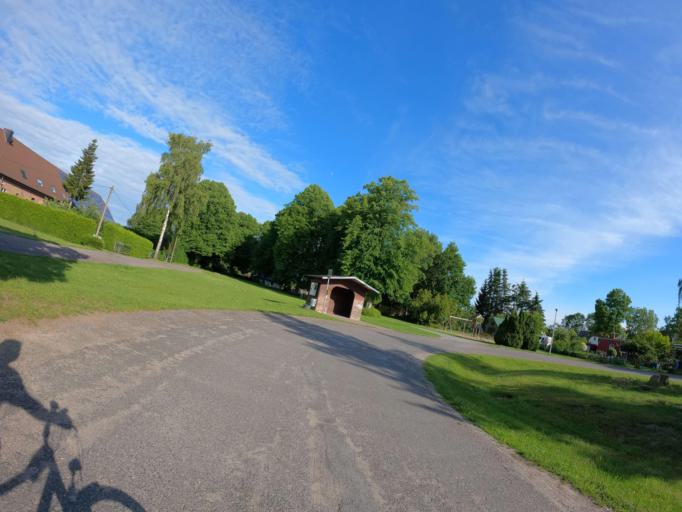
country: DE
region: Mecklenburg-Vorpommern
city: Altenpleen
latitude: 54.3321
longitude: 12.9702
